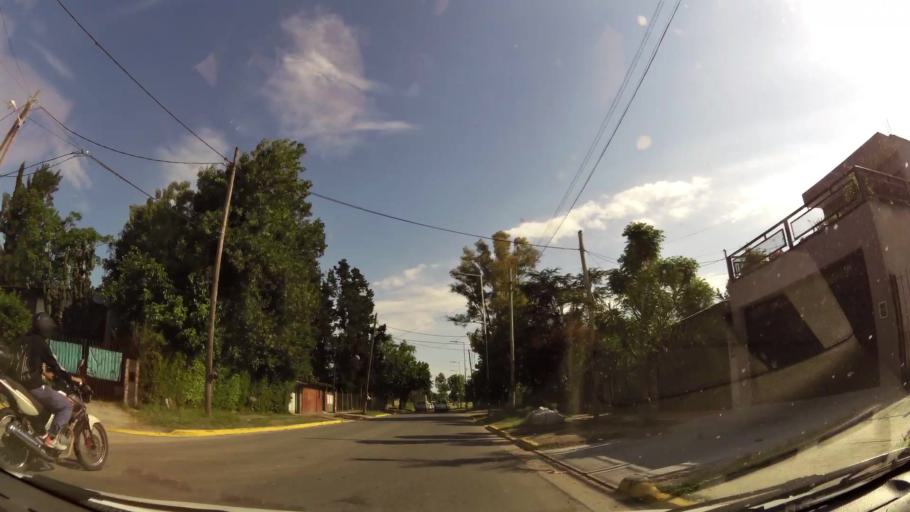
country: AR
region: Buenos Aires
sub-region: Partido de Merlo
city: Merlo
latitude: -34.6590
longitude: -58.7538
